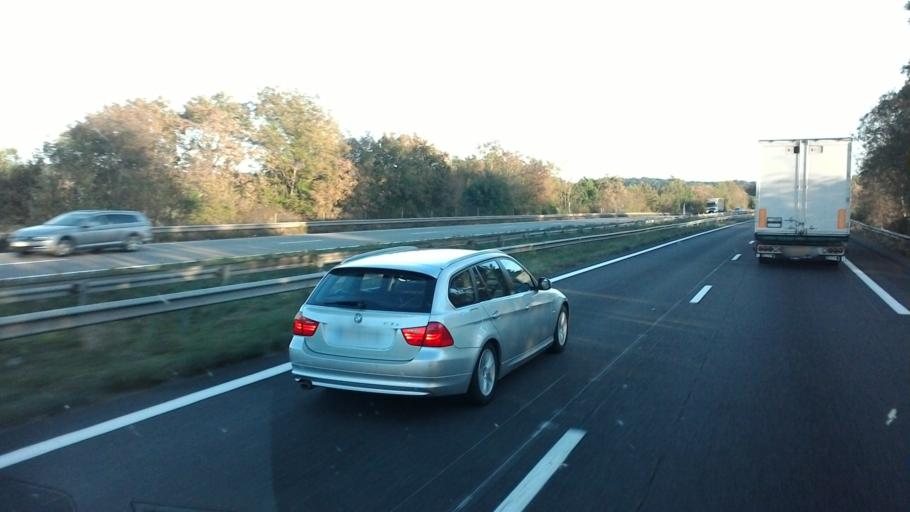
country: FR
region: Lorraine
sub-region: Departement de Meurthe-et-Moselle
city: Belleville
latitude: 48.8214
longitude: 6.1047
